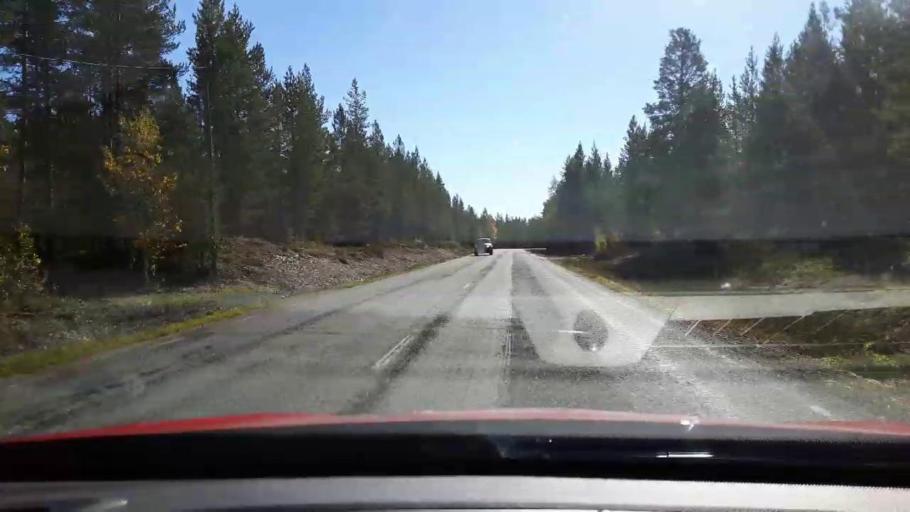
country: SE
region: Jaemtland
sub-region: Harjedalens Kommun
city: Sveg
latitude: 62.4241
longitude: 13.9020
